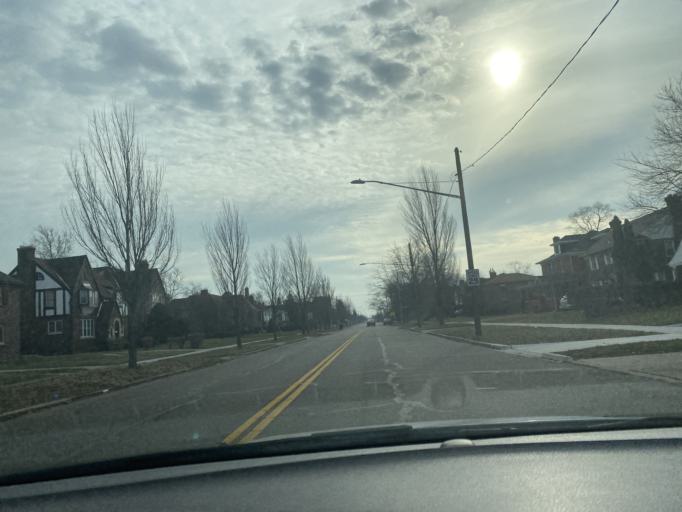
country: US
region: Michigan
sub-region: Wayne County
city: Highland Park
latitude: 42.3819
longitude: -83.1359
